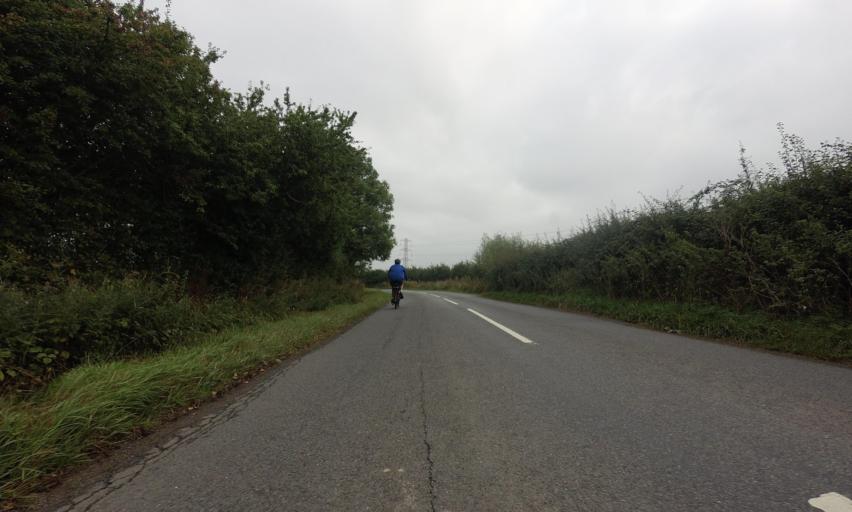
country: GB
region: England
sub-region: Gloucestershire
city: Gotherington
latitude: 51.9675
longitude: -2.0190
